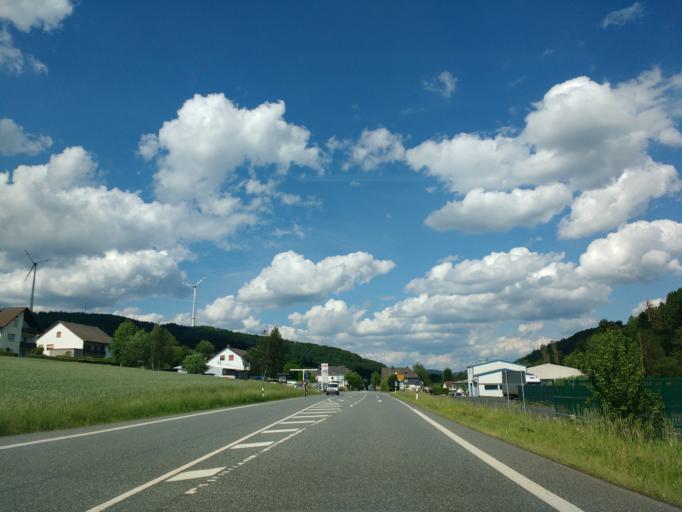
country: DE
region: Hesse
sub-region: Regierungsbezirk Giessen
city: Breidenbach
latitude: 50.8536
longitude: 8.4111
